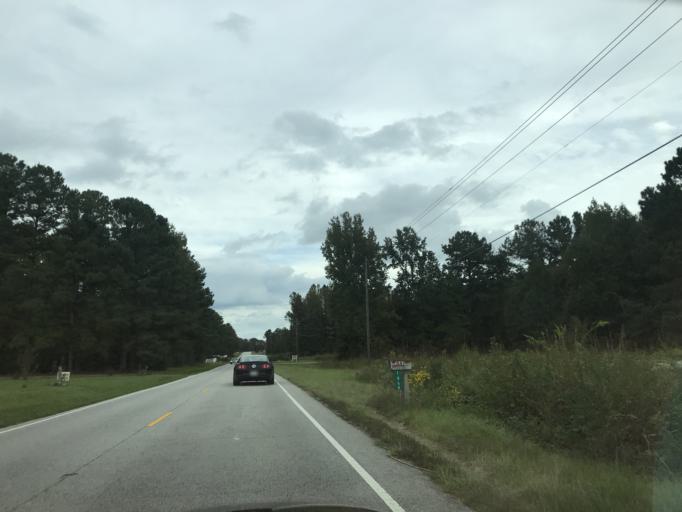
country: US
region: North Carolina
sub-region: Franklin County
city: Youngsville
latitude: 35.9950
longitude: -78.4131
